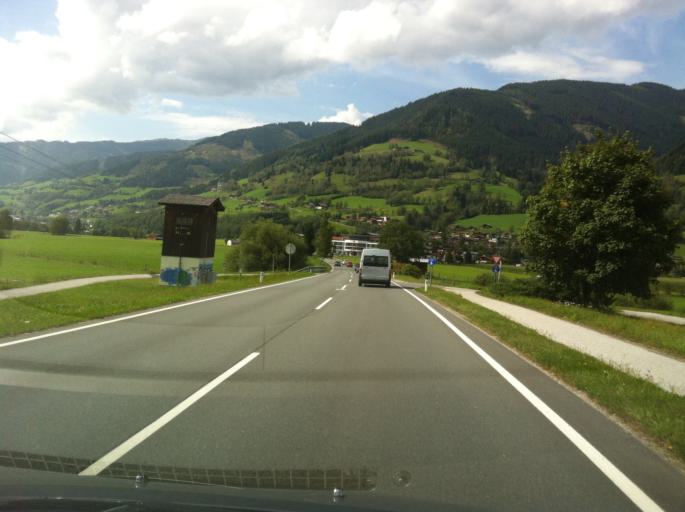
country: AT
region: Salzburg
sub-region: Politischer Bezirk Zell am See
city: Kaprun
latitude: 47.2847
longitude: 12.7515
